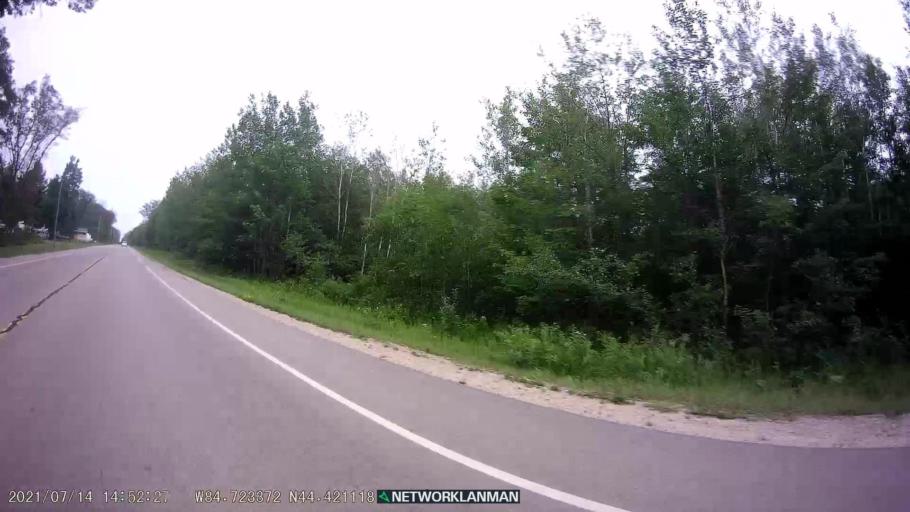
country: US
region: Michigan
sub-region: Roscommon County
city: Houghton Lake
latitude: 44.4211
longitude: -84.7228
